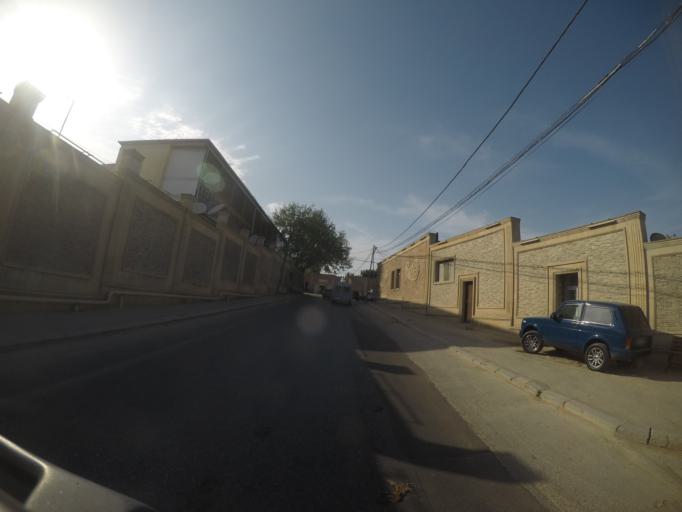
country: AZ
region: Baki
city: Binagadi
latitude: 40.4668
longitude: 49.8418
